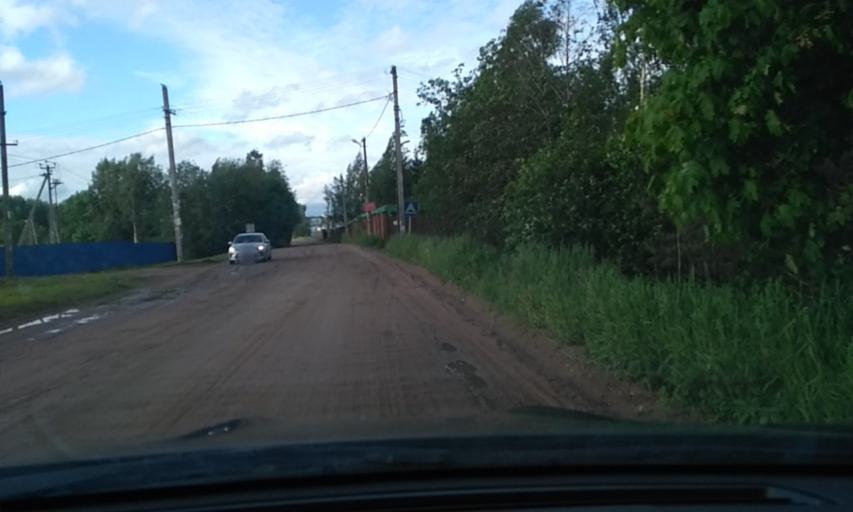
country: RU
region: Leningrad
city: Otradnoye
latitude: 59.7985
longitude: 30.8004
